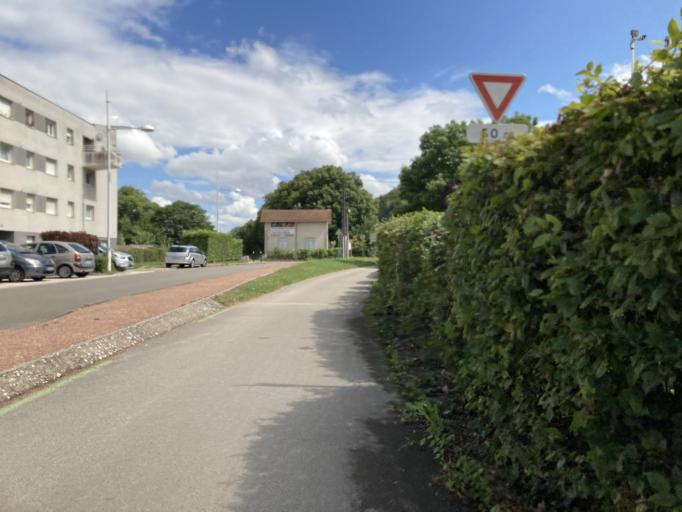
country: FR
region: Bourgogne
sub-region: Departement de la Cote-d'Or
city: Plombieres-les-Dijon
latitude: 47.3378
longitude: 4.9691
